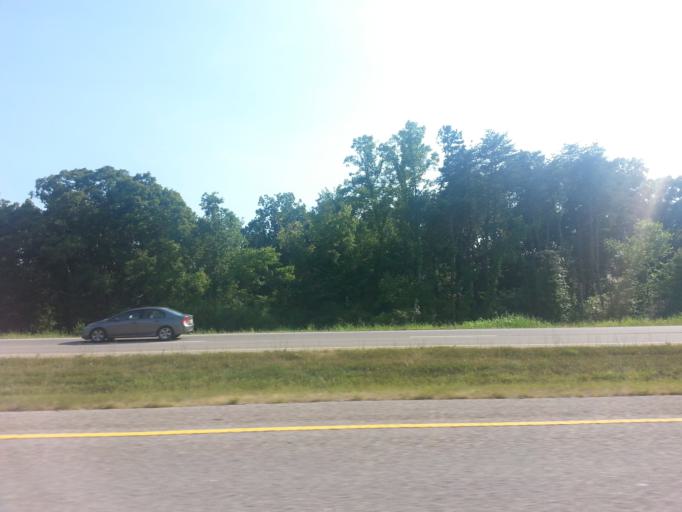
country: US
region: Tennessee
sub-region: Loudon County
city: Lenoir City
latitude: 35.7599
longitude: -84.2249
